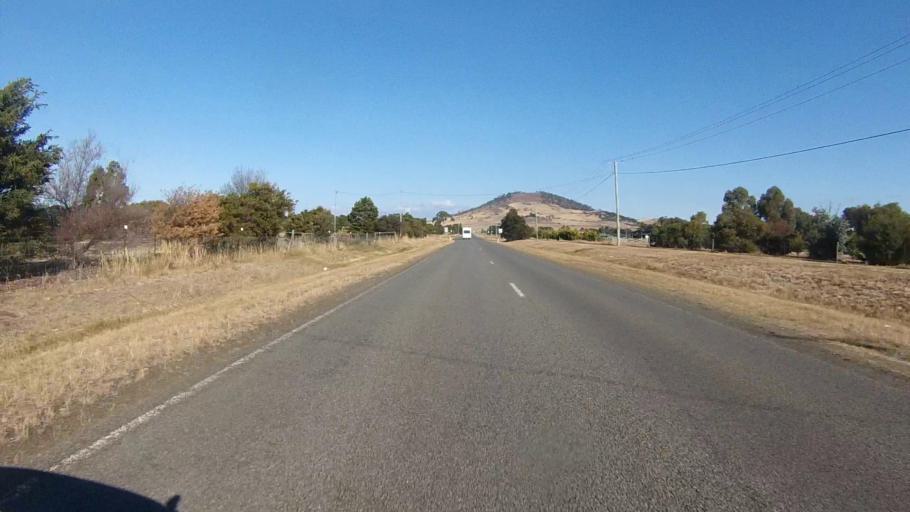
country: AU
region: Tasmania
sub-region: Clarence
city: Seven Mile Beach
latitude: -42.8521
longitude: 147.4859
